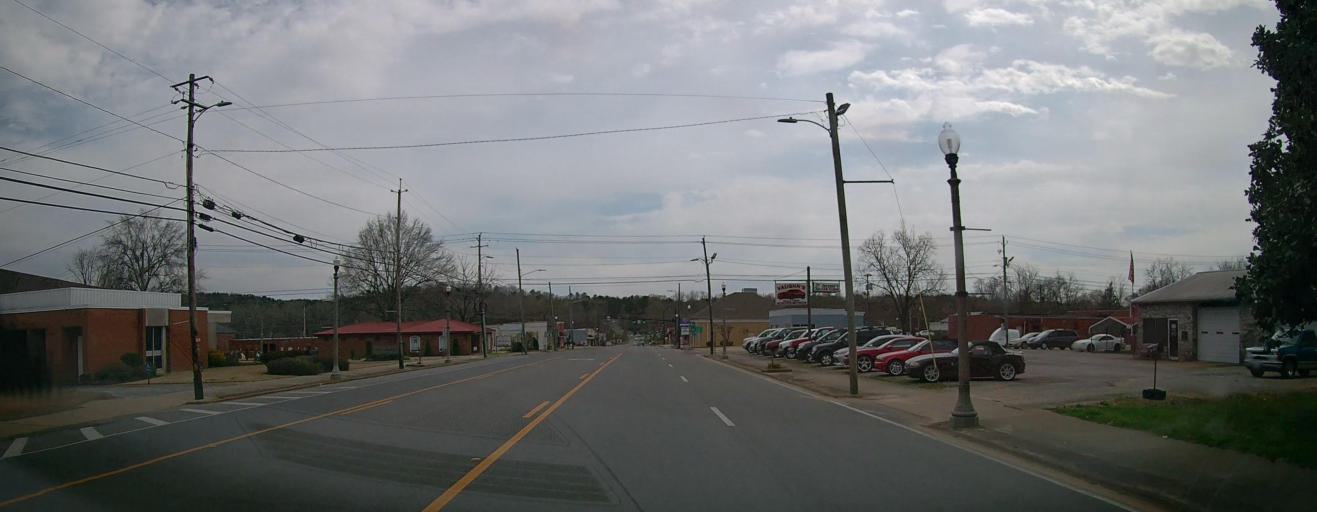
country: US
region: Alabama
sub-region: Marion County
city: Guin
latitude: 33.9674
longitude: -87.9151
